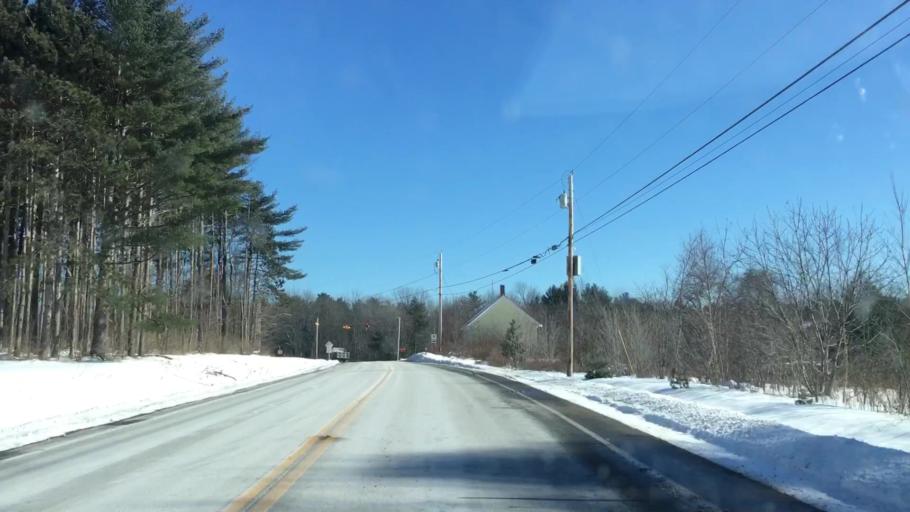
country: US
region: Maine
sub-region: Androscoggin County
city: Lisbon Falls
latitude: 44.0244
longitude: -70.0690
